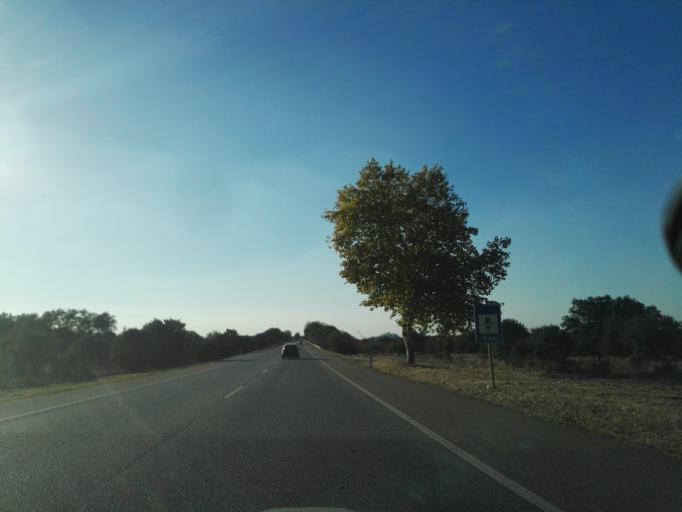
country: PT
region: Evora
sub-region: Estremoz
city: Estremoz
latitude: 38.8333
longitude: -7.5513
